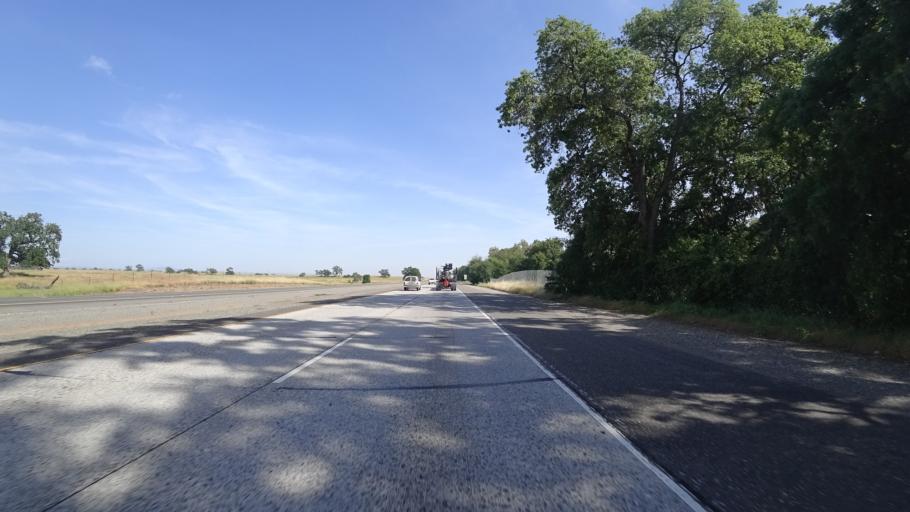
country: US
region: California
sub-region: Butte County
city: Durham
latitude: 39.6873
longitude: -121.7705
